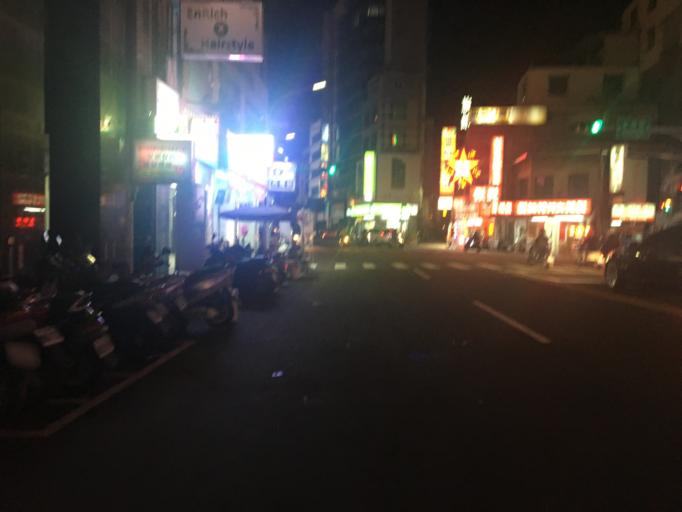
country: TW
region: Taiwan
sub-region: Hsinchu
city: Hsinchu
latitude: 24.8017
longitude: 120.9686
